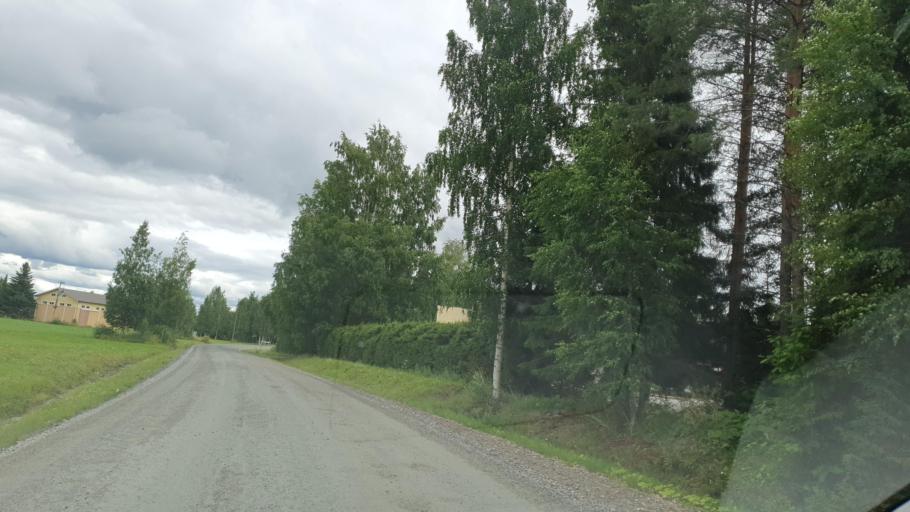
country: FI
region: Northern Savo
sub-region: Ylae-Savo
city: Iisalmi
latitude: 63.5369
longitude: 27.0789
